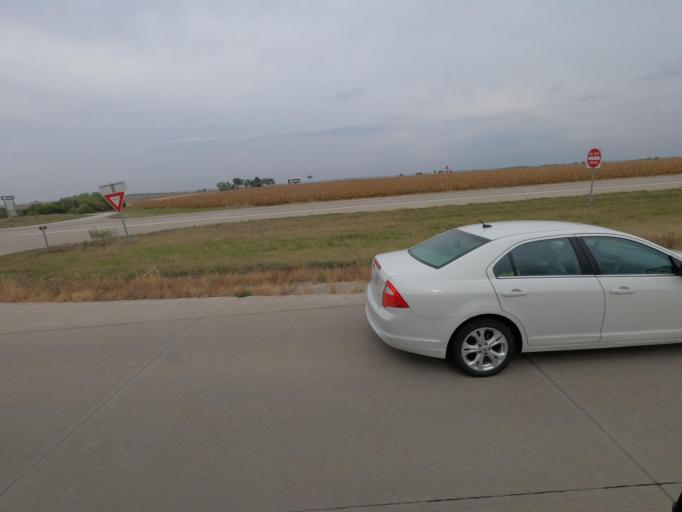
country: US
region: Iowa
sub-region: Mahaska County
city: Oskaloosa
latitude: 41.3594
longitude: -92.7749
